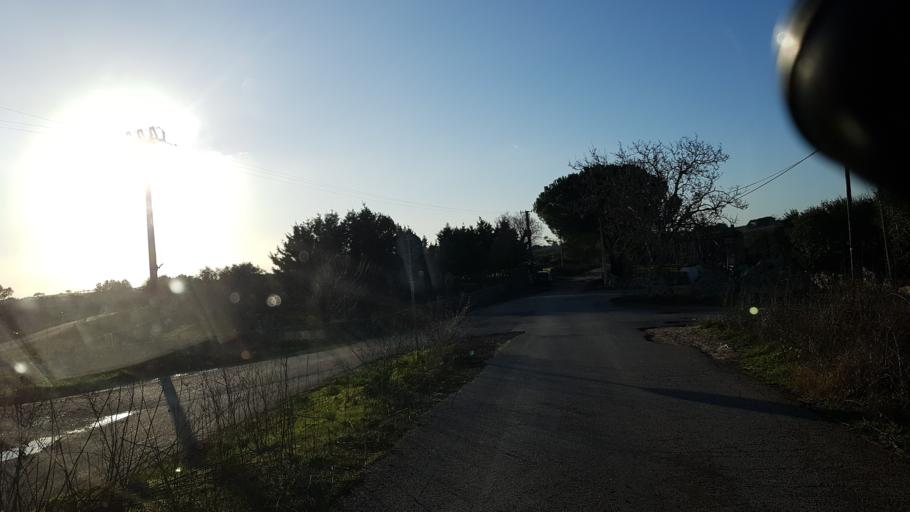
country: IT
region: Apulia
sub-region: Provincia di Bari
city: Gioia del Colle
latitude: 40.8004
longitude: 16.8973
